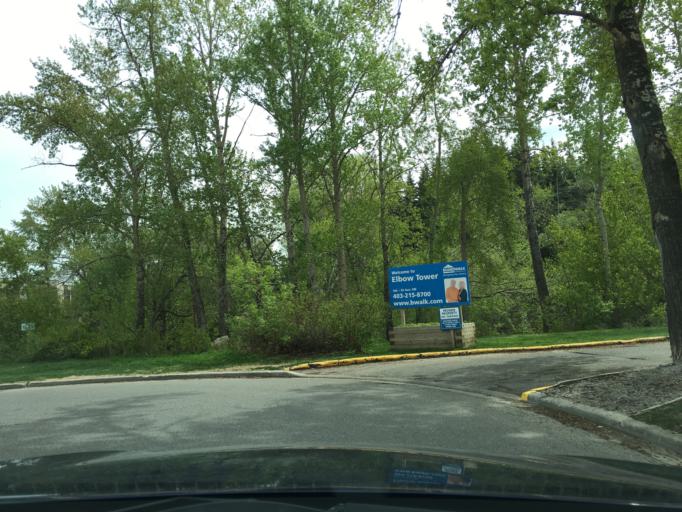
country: CA
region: Alberta
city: Calgary
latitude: 51.0294
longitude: -114.0642
